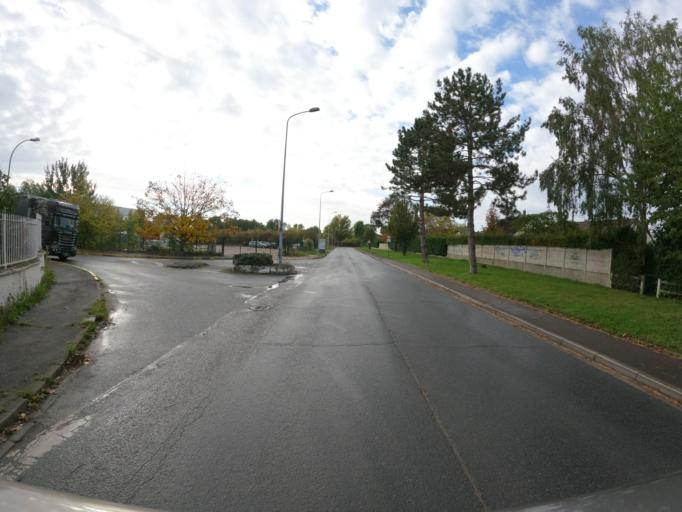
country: FR
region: Ile-de-France
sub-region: Departement de Seine-et-Marne
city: Courtry
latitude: 48.9075
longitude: 2.6030
